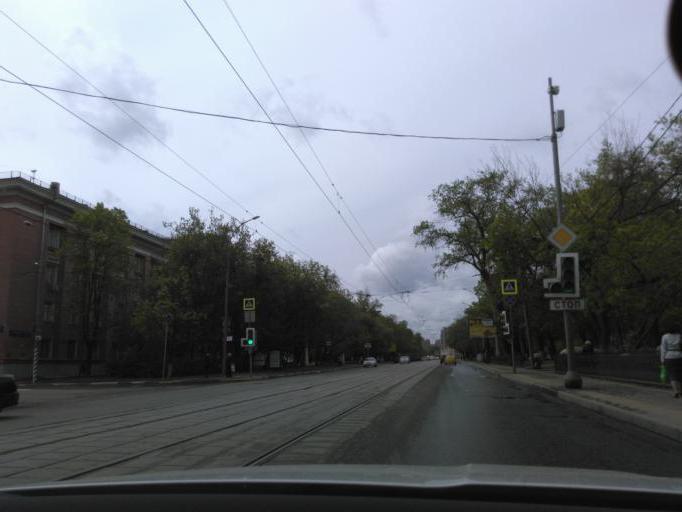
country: RU
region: Moscow
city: Taganskiy
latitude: 55.7436
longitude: 37.6771
